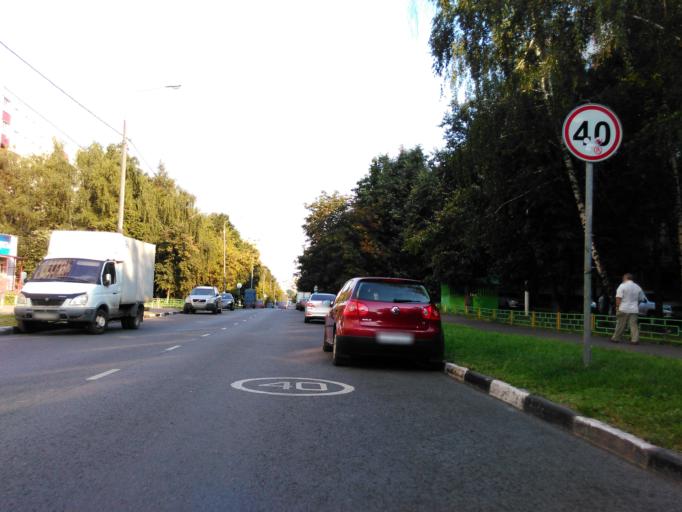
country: RU
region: Moskovskaya
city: Cheremushki
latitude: 55.6454
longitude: 37.5328
